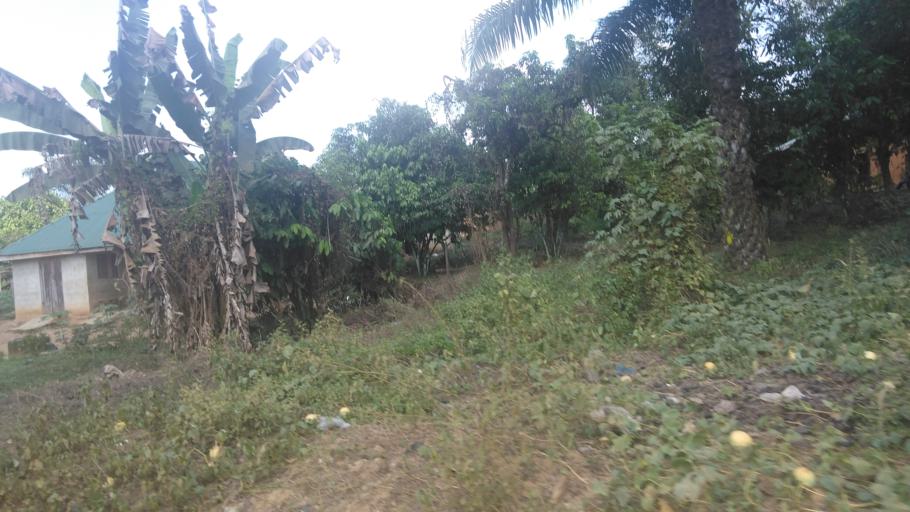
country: NG
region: Osun
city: Ifetedo
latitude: 7.0127
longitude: 4.6354
